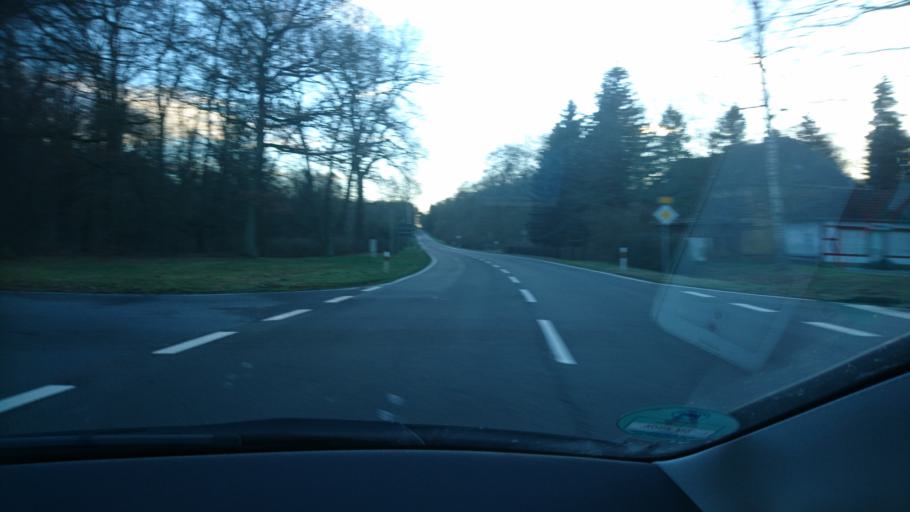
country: DE
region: Saxony
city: Bad Duben
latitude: 51.6565
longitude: 12.5917
